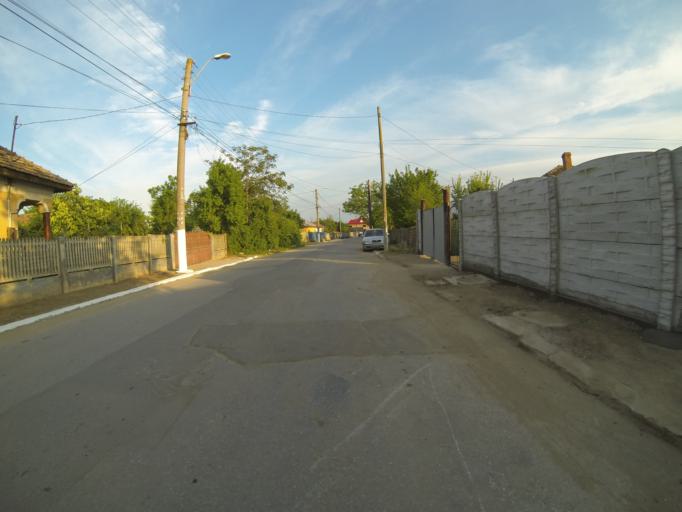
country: RO
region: Dolj
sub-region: Comuna Segarcea
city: Segarcea
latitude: 44.0966
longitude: 23.7501
